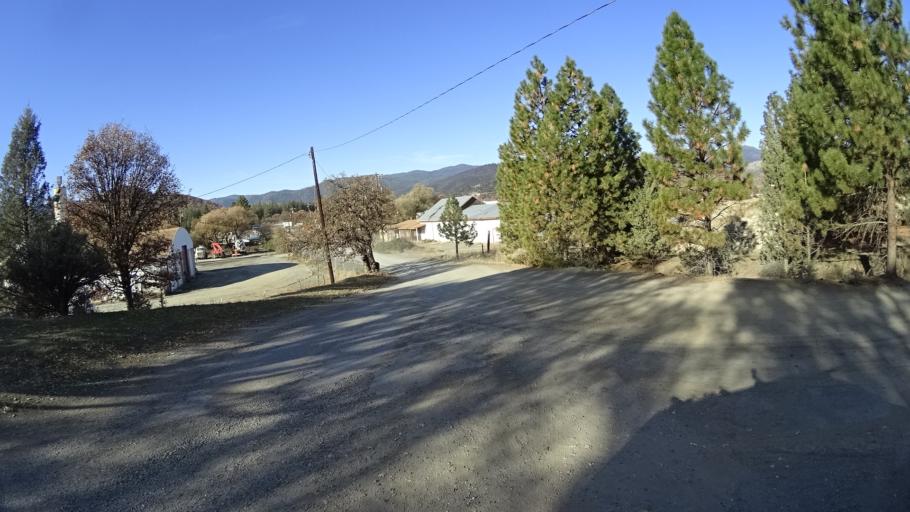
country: US
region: California
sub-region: Siskiyou County
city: Yreka
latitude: 41.6919
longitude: -122.6349
